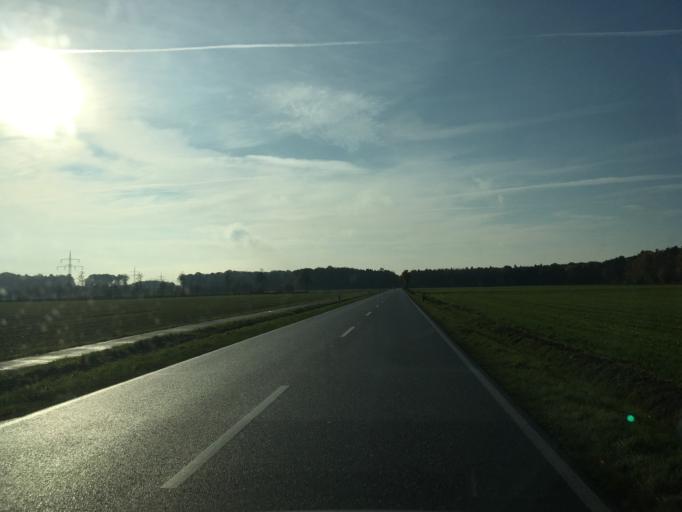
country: DE
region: North Rhine-Westphalia
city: Stadtlohn
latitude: 52.0308
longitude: 6.9576
